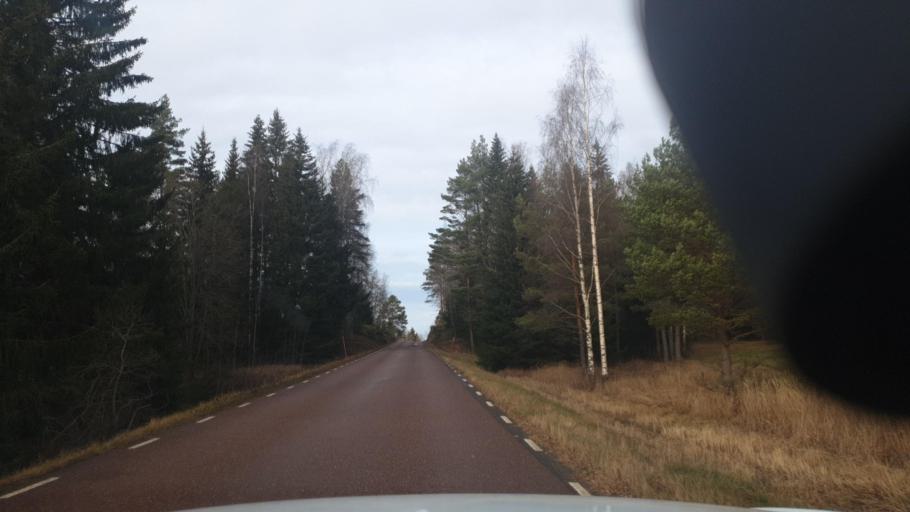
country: NO
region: Ostfold
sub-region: Romskog
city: Romskog
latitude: 59.7378
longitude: 12.0592
